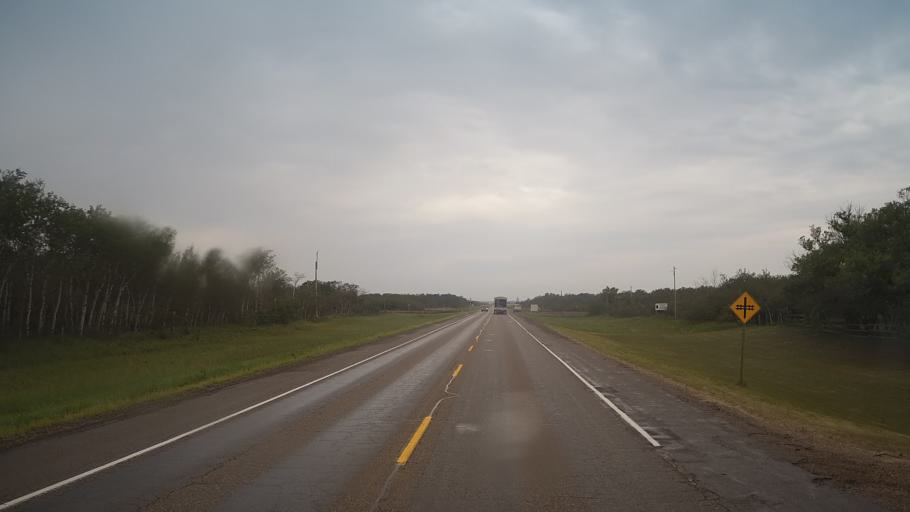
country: CA
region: Saskatchewan
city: Langham
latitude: 52.1294
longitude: -107.0470
